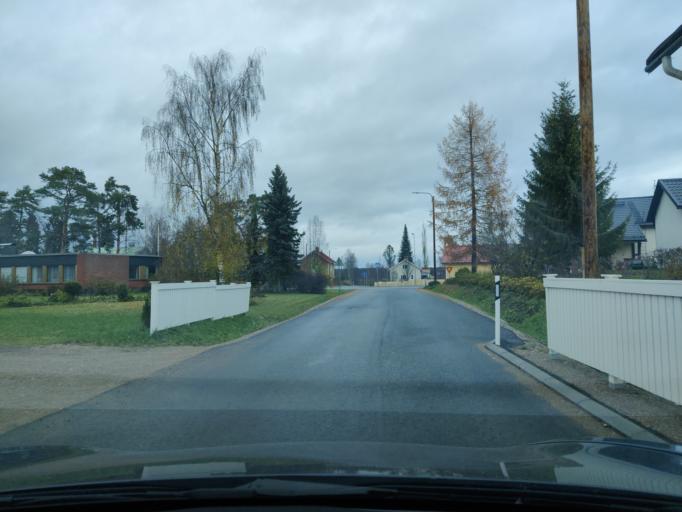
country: FI
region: Northern Savo
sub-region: Ylae-Savo
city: Kiuruvesi
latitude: 63.6490
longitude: 26.6338
